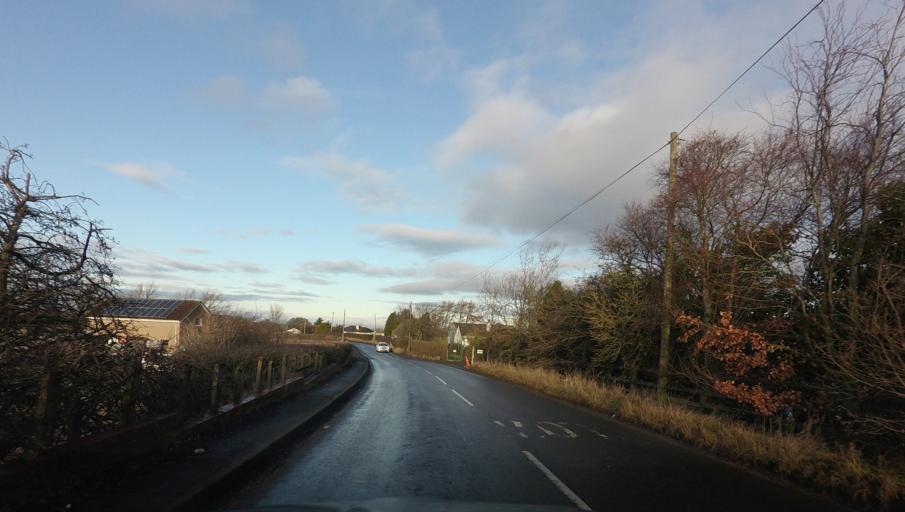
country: GB
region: Scotland
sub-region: West Lothian
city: East Calder
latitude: 55.8962
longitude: -3.4431
